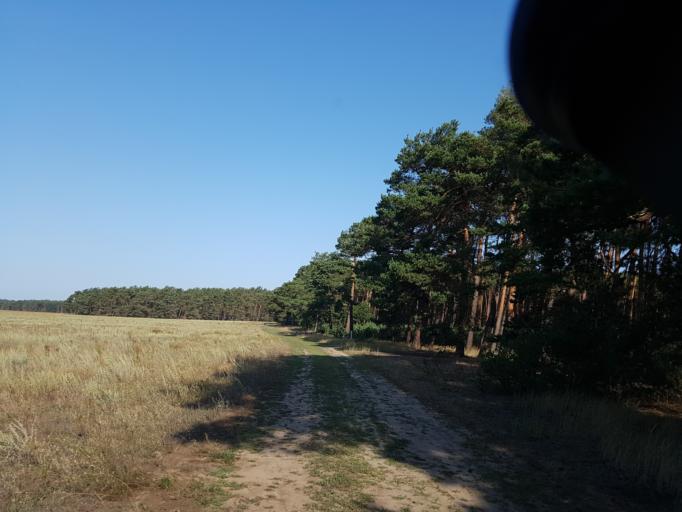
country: DE
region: Brandenburg
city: Wollin
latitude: 52.2492
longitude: 12.5087
